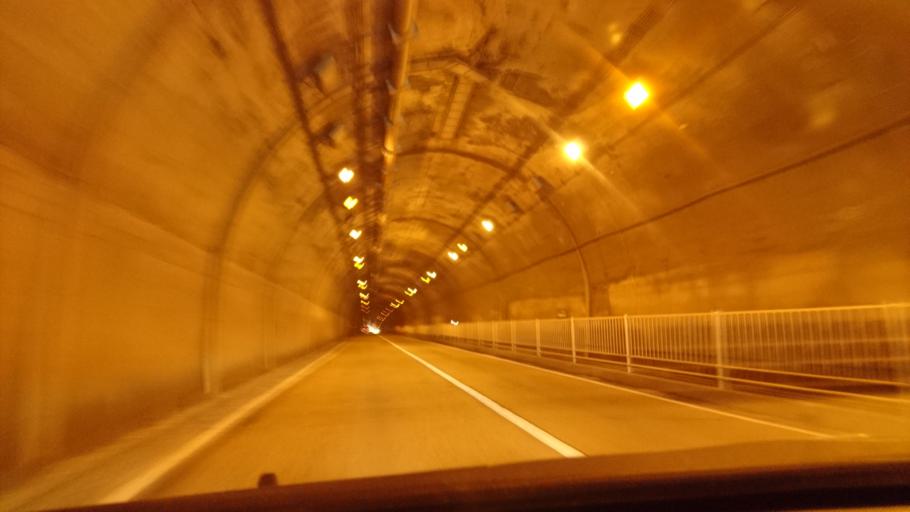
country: JP
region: Iwate
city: Kamaishi
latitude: 39.1984
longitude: 141.8613
